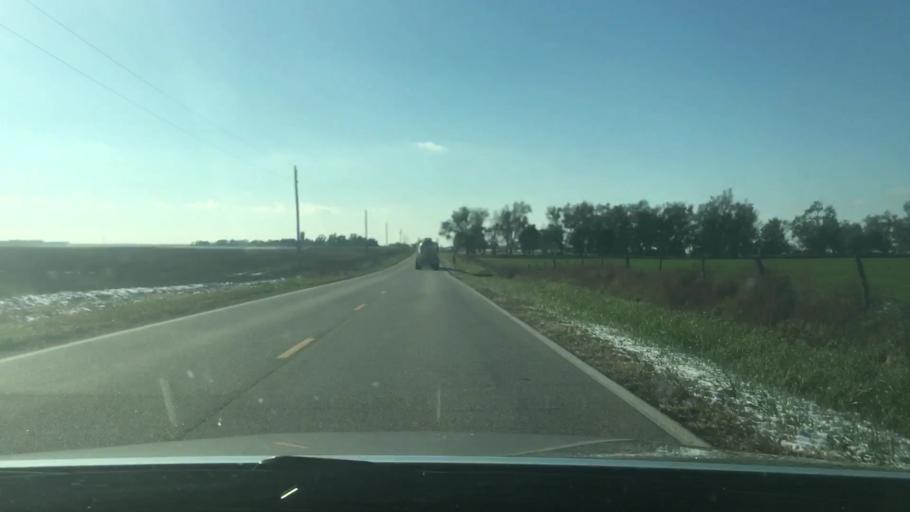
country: US
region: Kansas
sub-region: Rice County
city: Sterling
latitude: 38.1448
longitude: -98.1715
